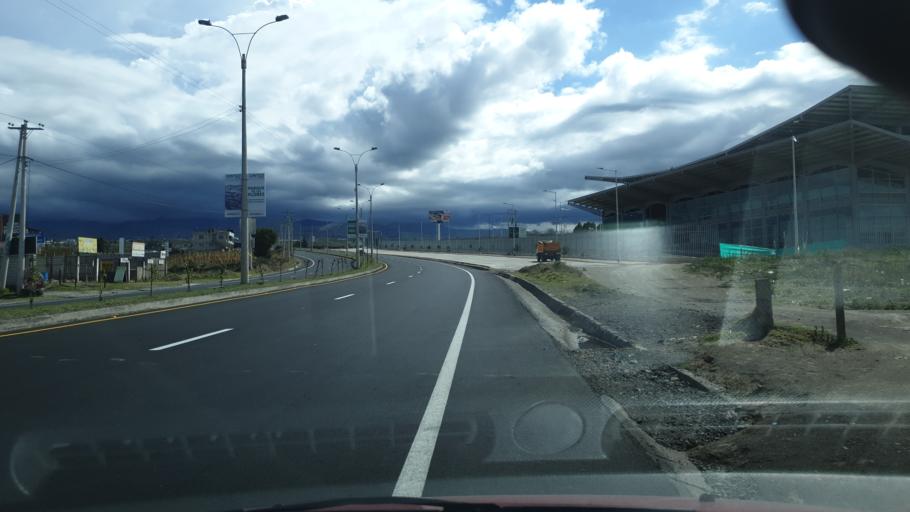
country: EC
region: Tungurahua
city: Ambato
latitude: -1.3007
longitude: -78.6329
